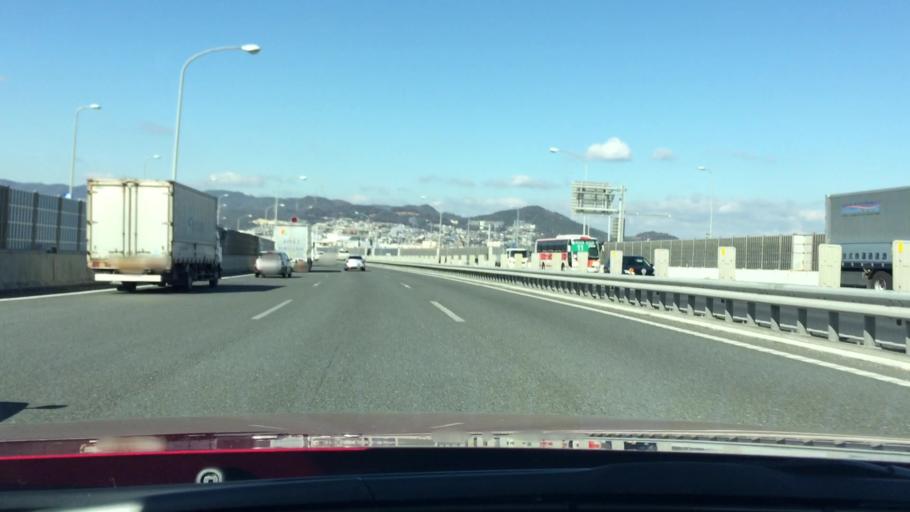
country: JP
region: Osaka
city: Ikeda
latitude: 34.8066
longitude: 135.4316
